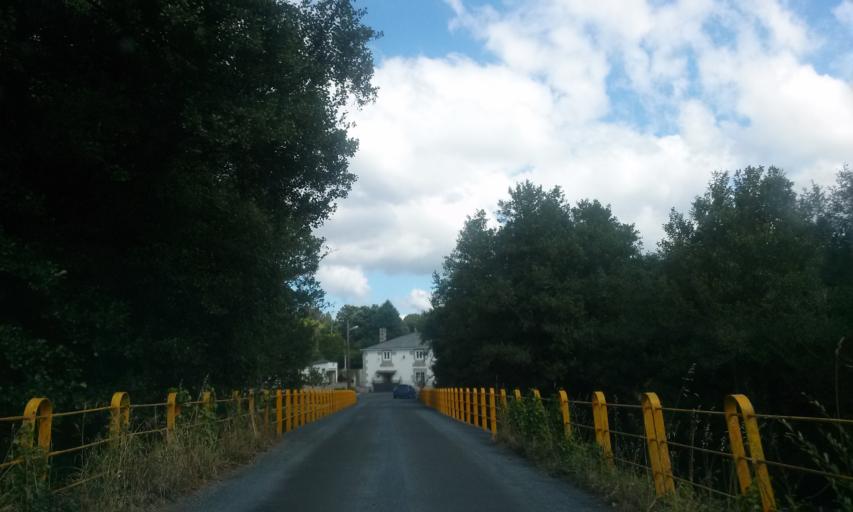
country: ES
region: Galicia
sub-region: Provincia de Lugo
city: Rabade
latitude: 43.1163
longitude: -7.6568
